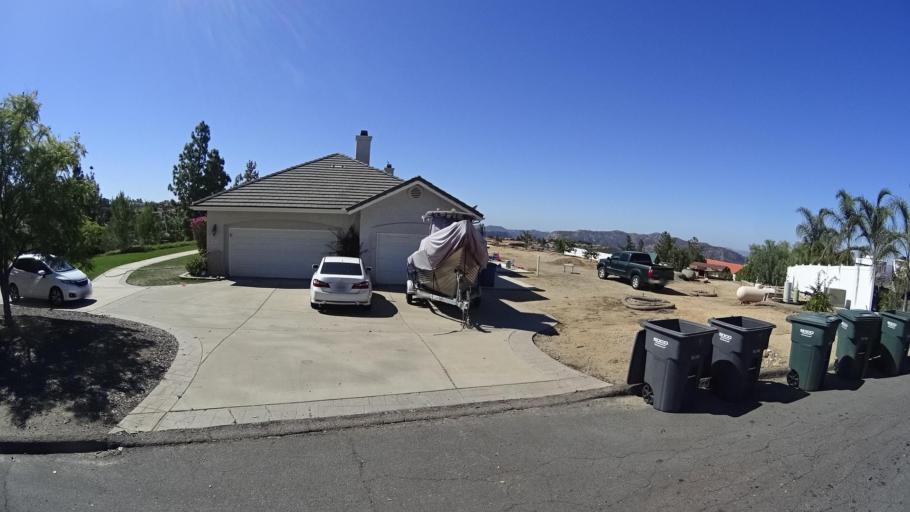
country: US
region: California
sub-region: San Diego County
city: Alpine
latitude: 32.8524
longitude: -116.7653
